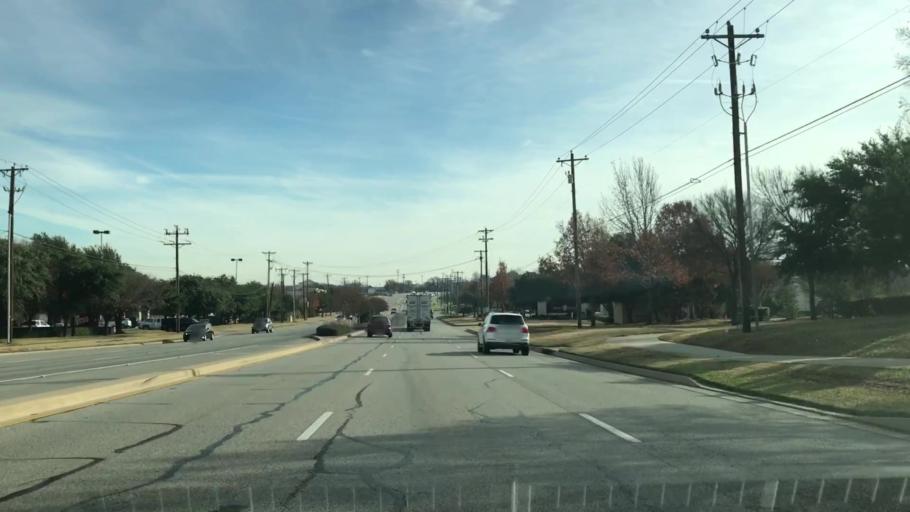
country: US
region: Texas
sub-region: Tarrant County
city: Southlake
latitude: 32.9409
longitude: -97.1221
